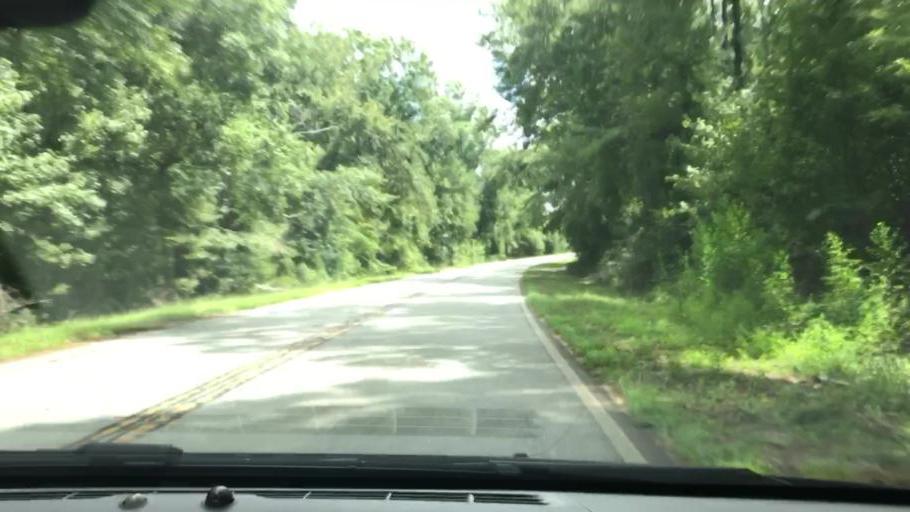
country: US
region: Georgia
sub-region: Quitman County
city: Georgetown
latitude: 32.0380
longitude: -85.0284
